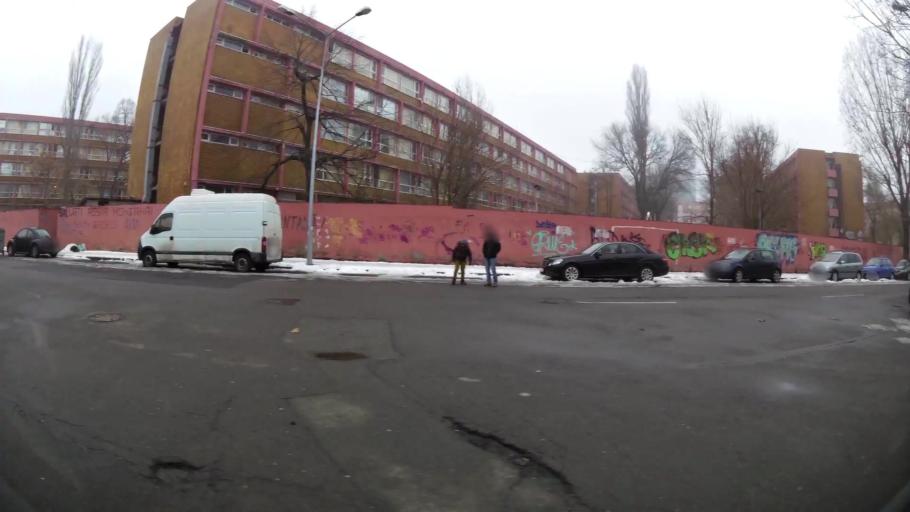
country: RO
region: Bucuresti
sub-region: Municipiul Bucuresti
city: Bucuresti
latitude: 44.4462
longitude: 26.0567
